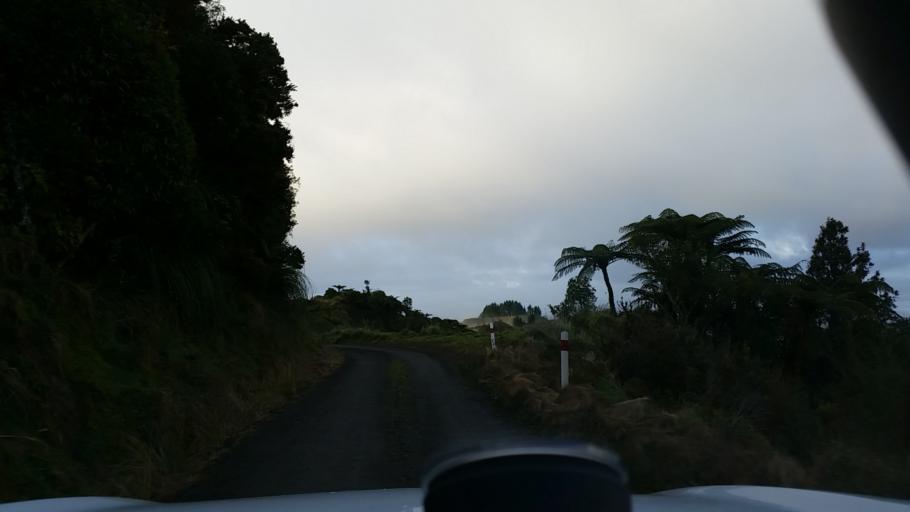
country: NZ
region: Taranaki
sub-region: South Taranaki District
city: Eltham
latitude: -39.4497
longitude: 174.4562
